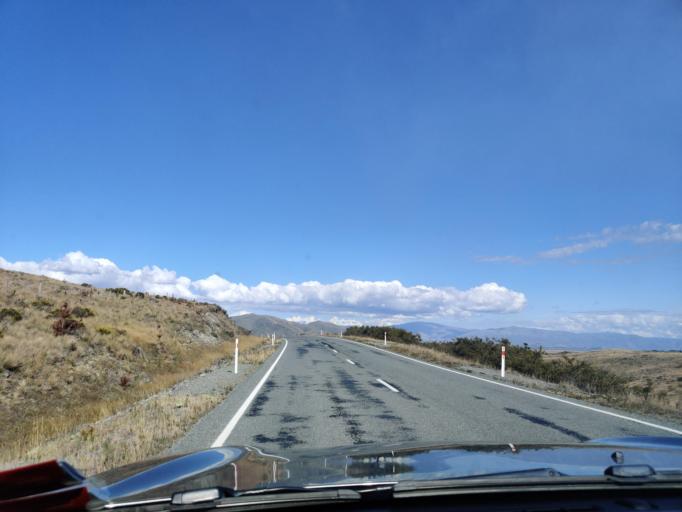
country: NZ
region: Canterbury
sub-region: Timaru District
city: Pleasant Point
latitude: -44.1844
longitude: 170.2327
